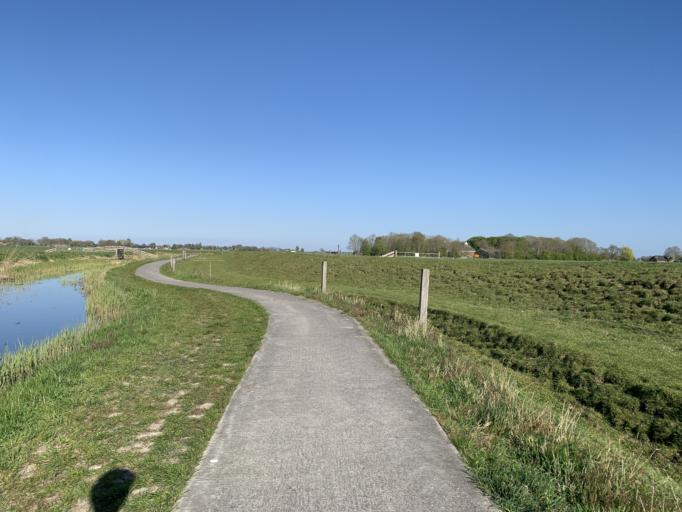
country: NL
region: Groningen
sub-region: Gemeente Winsum
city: Winsum
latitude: 53.2895
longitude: 6.5093
